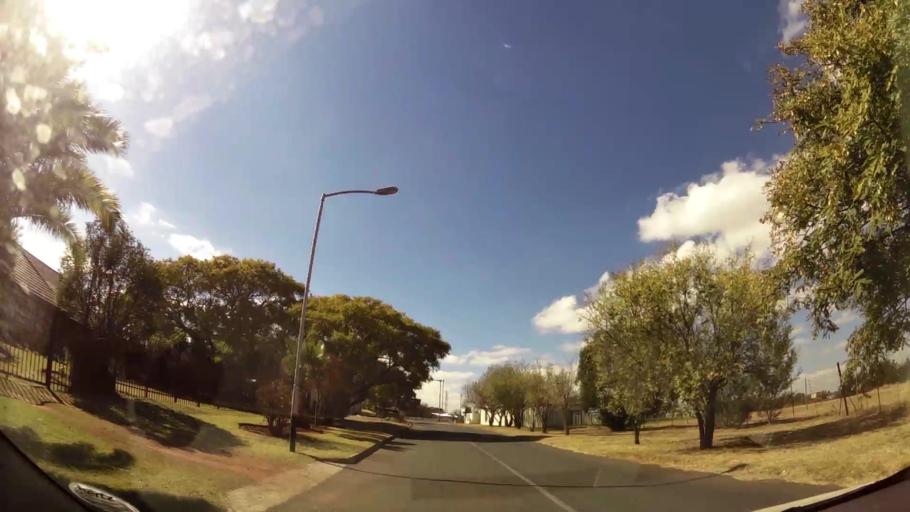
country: ZA
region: Gauteng
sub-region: West Rand District Municipality
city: Krugersdorp
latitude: -26.1074
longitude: 27.8008
